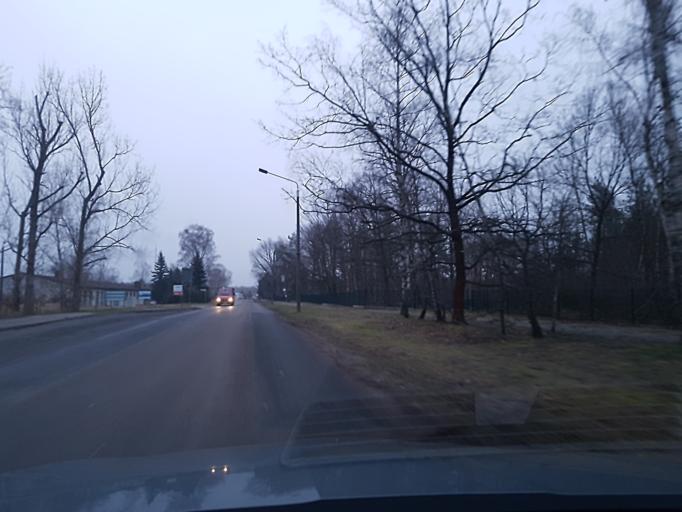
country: DE
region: Brandenburg
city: Doberlug-Kirchhain
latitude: 51.6274
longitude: 13.5770
